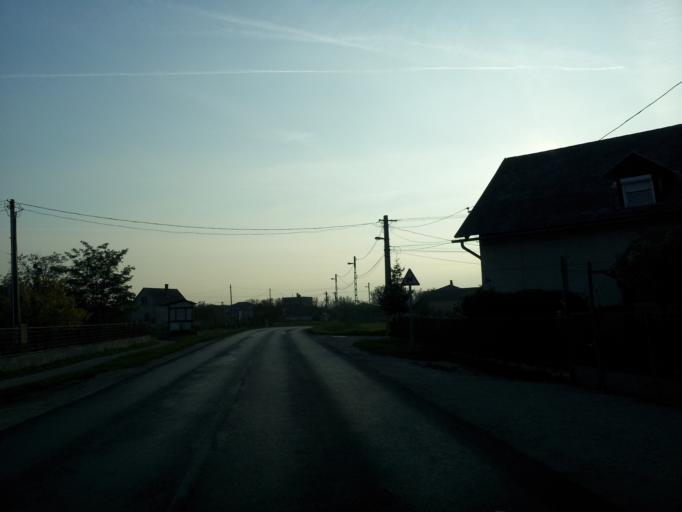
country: HU
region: Komarom-Esztergom
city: Kisber
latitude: 47.4973
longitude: 18.0160
